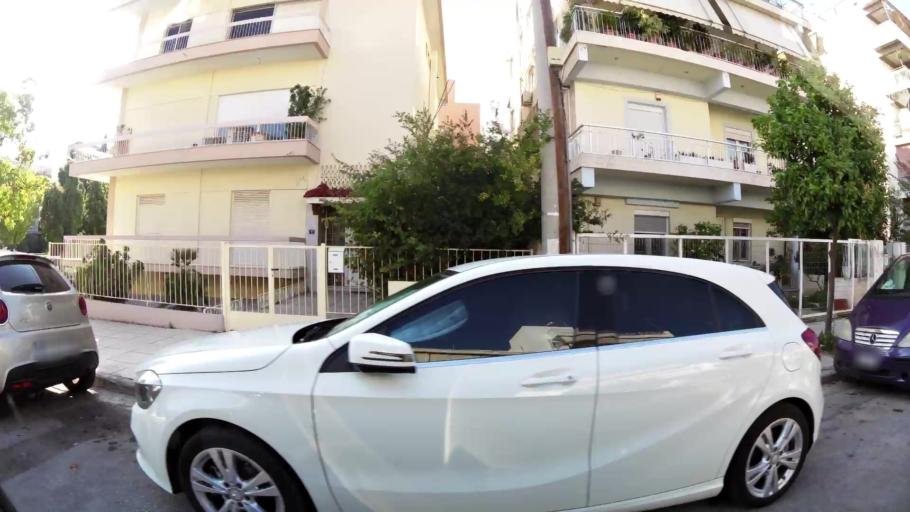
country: GR
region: Attica
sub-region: Nomarchia Athinas
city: Argyroupoli
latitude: 37.9062
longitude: 23.7482
